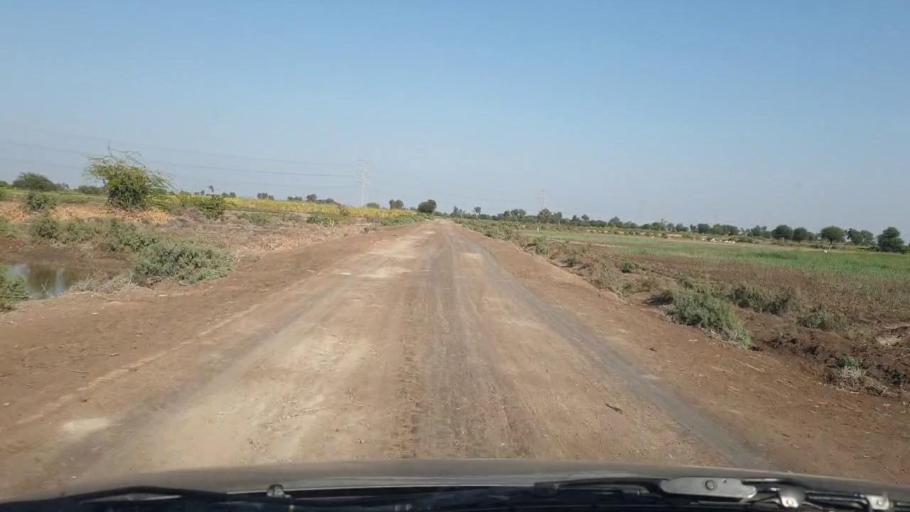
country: PK
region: Sindh
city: Digri
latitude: 25.1608
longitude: 69.2763
